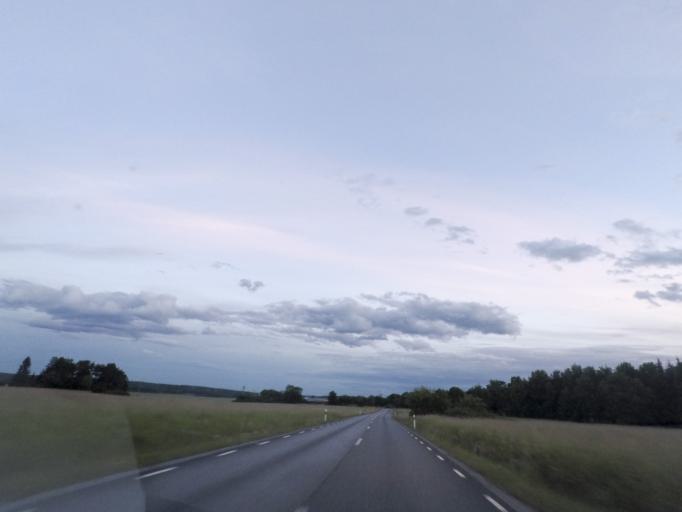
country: SE
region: Uppsala
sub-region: Habo Kommun
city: Balsta
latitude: 59.6492
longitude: 17.5385
